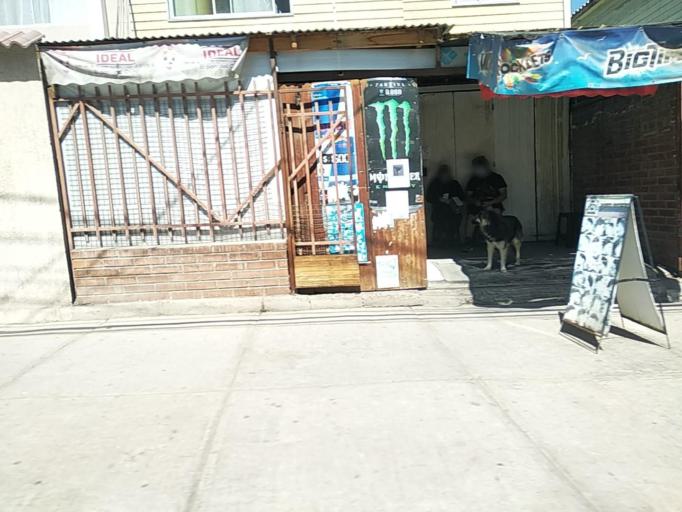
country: CL
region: Atacama
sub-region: Provincia de Copiapo
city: Copiapo
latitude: -27.4078
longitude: -70.2863
